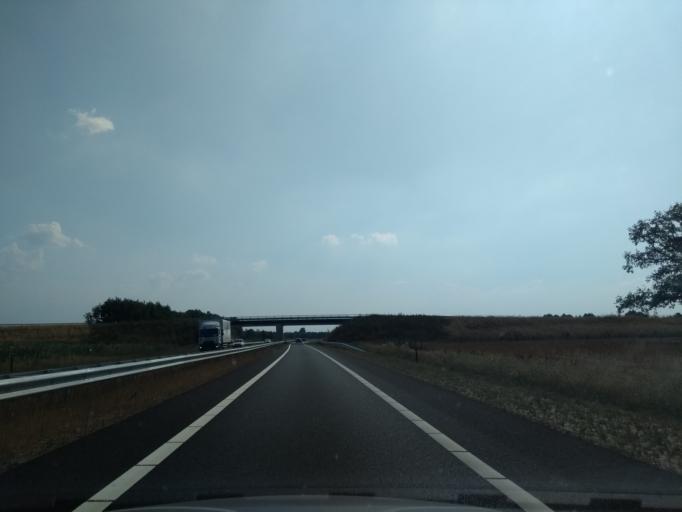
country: NL
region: Overijssel
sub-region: Gemeente Haaksbergen
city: Haaksbergen
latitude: 52.1715
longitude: 6.7134
